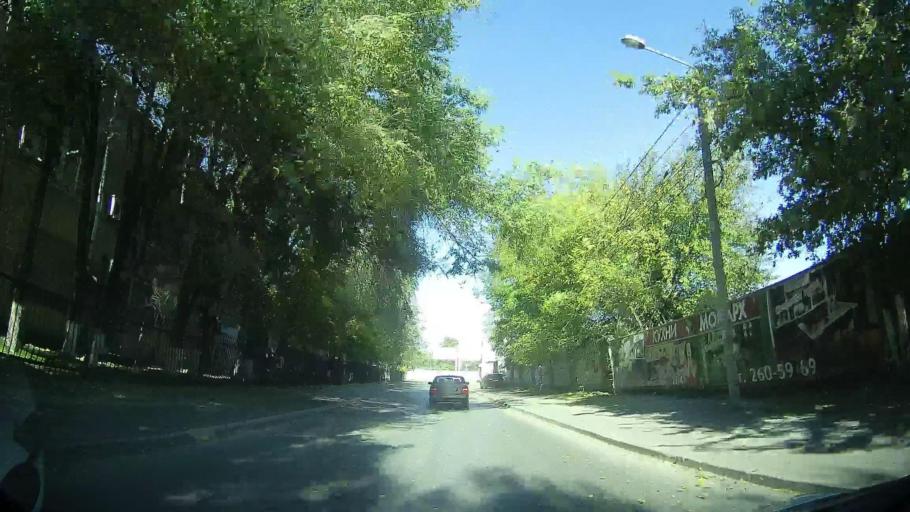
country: RU
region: Rostov
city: Rostov-na-Donu
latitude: 47.2359
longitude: 39.7178
